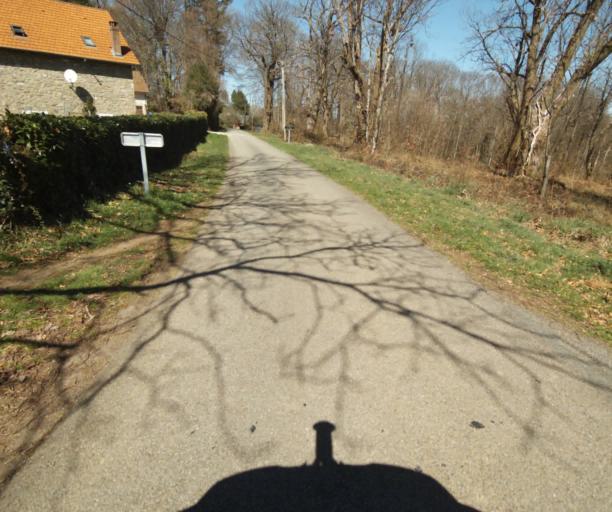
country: FR
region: Limousin
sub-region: Departement de la Correze
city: Uzerche
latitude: 45.3879
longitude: 1.6067
